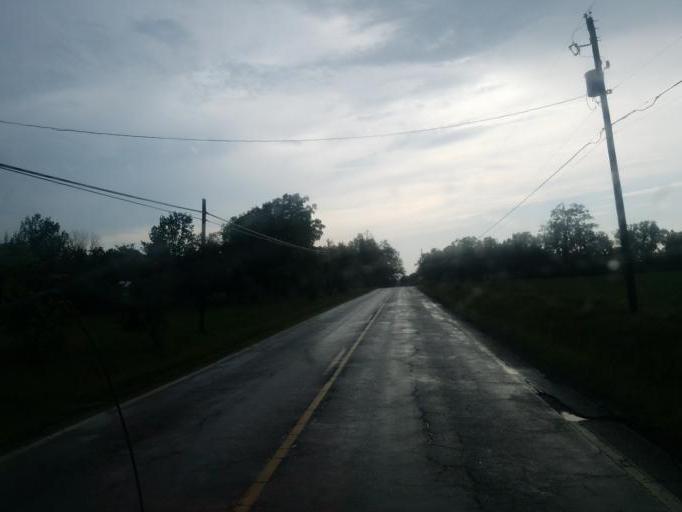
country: US
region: Ohio
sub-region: Wayne County
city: Creston
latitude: 40.9450
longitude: -81.9259
